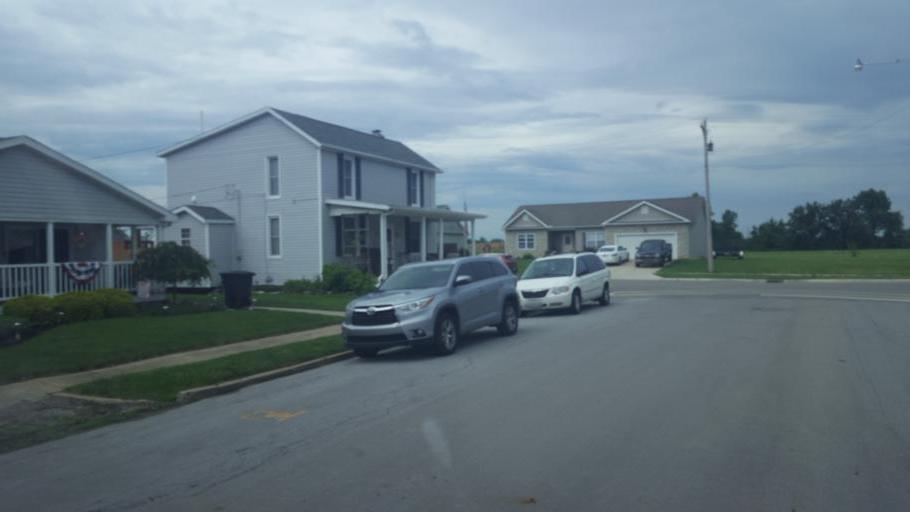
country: US
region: Ohio
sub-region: Pickaway County
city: Ashville
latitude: 39.7179
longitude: -82.9570
